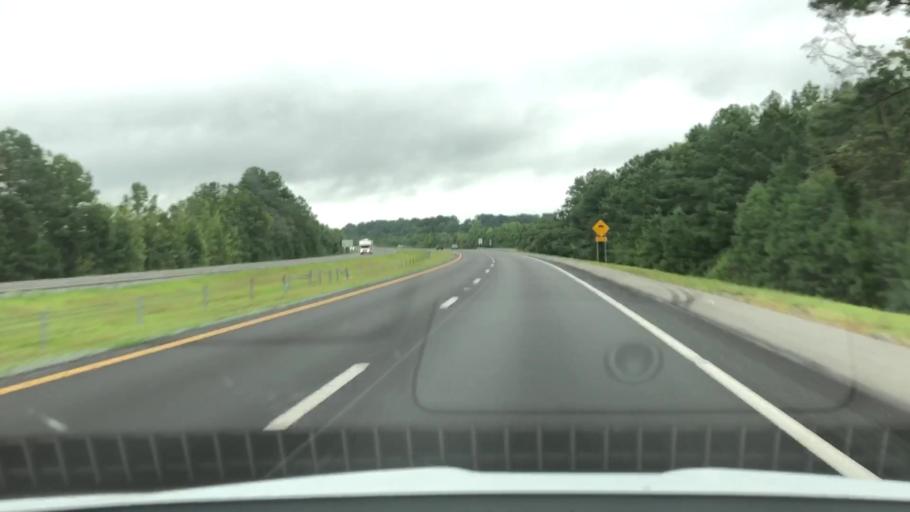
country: US
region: North Carolina
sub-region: Wayne County
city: Goldsboro
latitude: 35.4334
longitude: -77.9864
